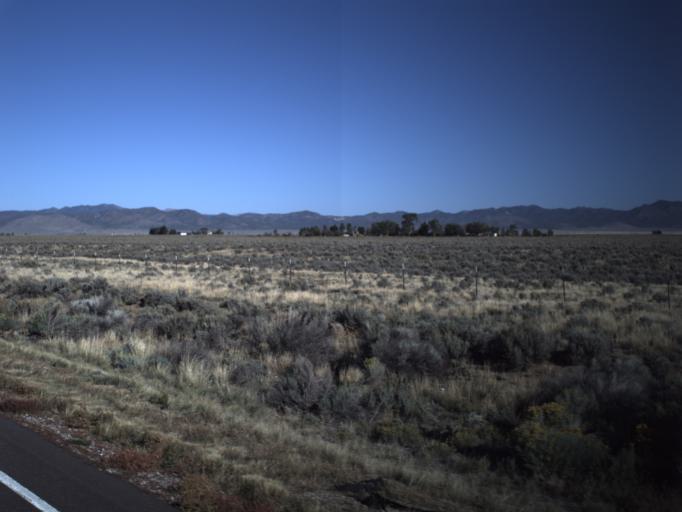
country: US
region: Utah
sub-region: Washington County
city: Enterprise
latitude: 37.7608
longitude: -113.8010
